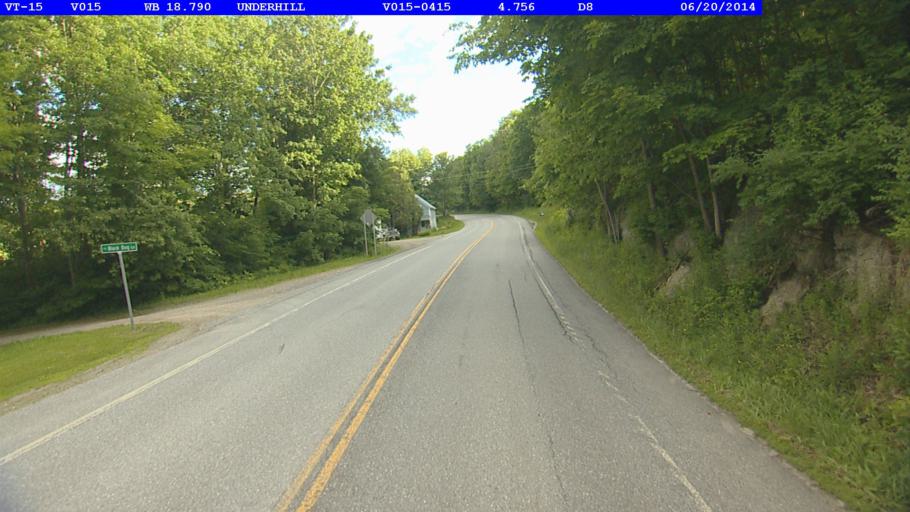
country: US
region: Vermont
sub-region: Chittenden County
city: Jericho
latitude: 44.5918
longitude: -72.9378
